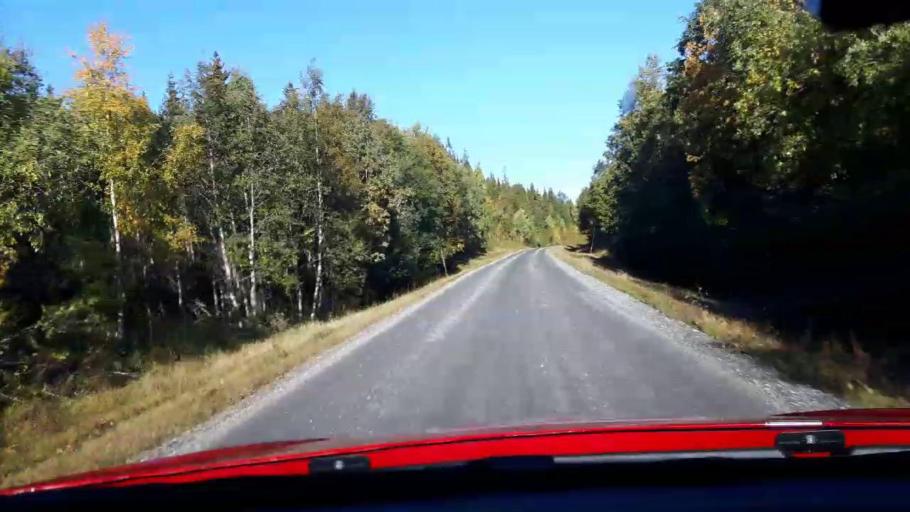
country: NO
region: Nord-Trondelag
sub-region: Lierne
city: Sandvika
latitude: 64.5741
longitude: 13.8994
